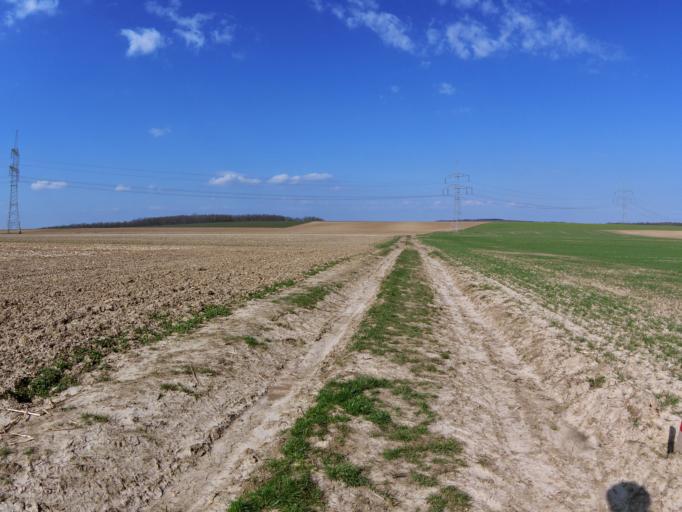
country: DE
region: Bavaria
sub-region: Regierungsbezirk Unterfranken
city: Rottendorf
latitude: 49.7953
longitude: 10.0656
